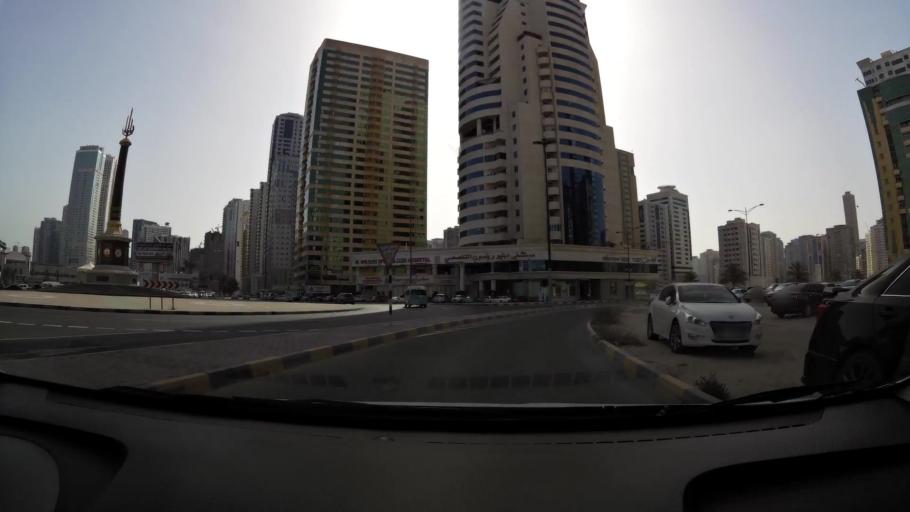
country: AE
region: Ash Shariqah
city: Sharjah
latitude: 25.3083
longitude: 55.3703
